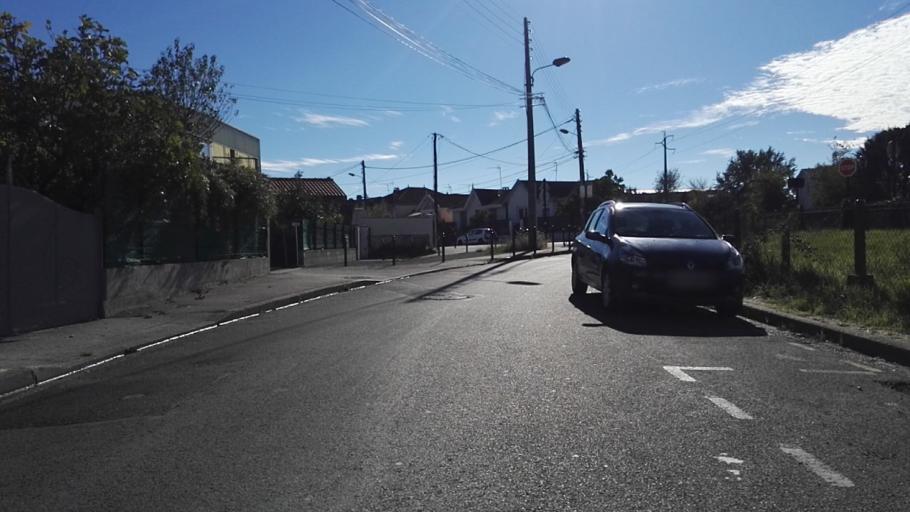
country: FR
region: Aquitaine
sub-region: Departement de la Gironde
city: Bruges
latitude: 44.8609
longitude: -0.6256
